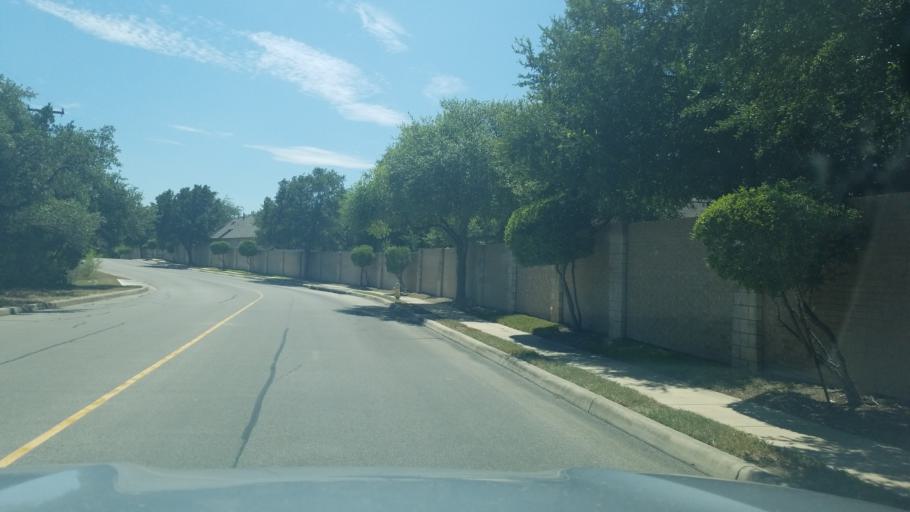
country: US
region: Texas
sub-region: Bexar County
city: Timberwood Park
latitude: 29.6597
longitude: -98.5074
